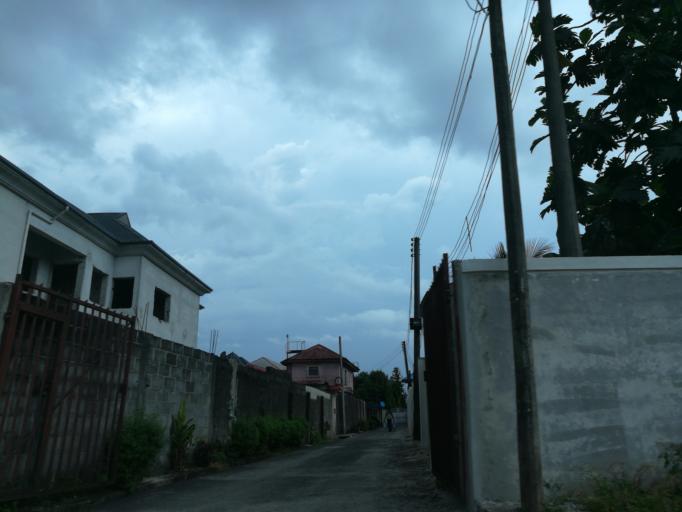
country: NG
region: Rivers
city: Port Harcourt
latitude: 4.8211
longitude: 7.0665
